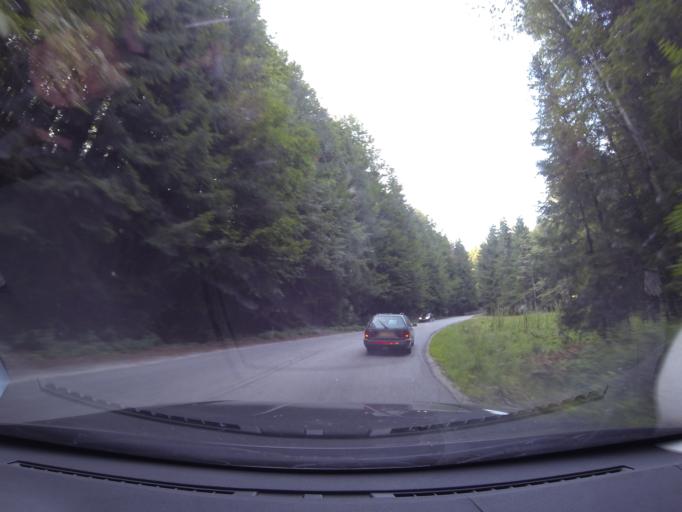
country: RO
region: Arges
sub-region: Comuna Arefu
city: Arefu
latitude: 45.4057
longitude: 24.6373
